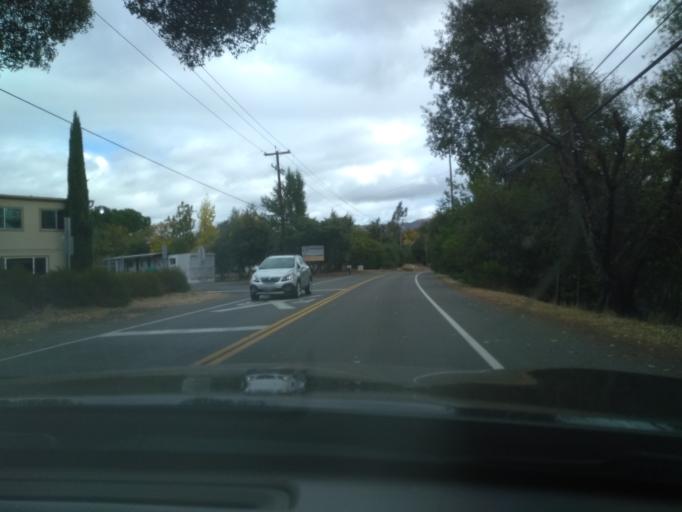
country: US
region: California
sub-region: Mendocino County
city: Ukiah
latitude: 39.1939
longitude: -123.2034
